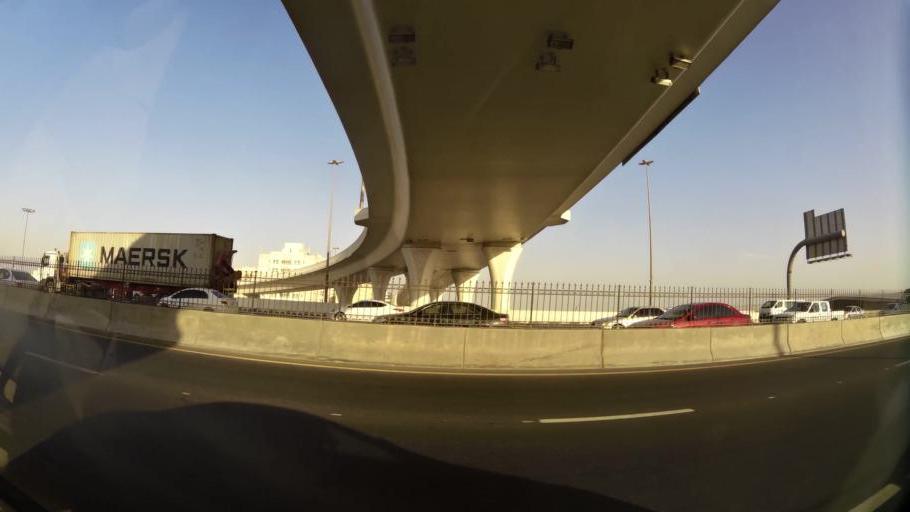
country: AE
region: Ash Shariqah
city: Sharjah
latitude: 25.2965
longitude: 55.4368
